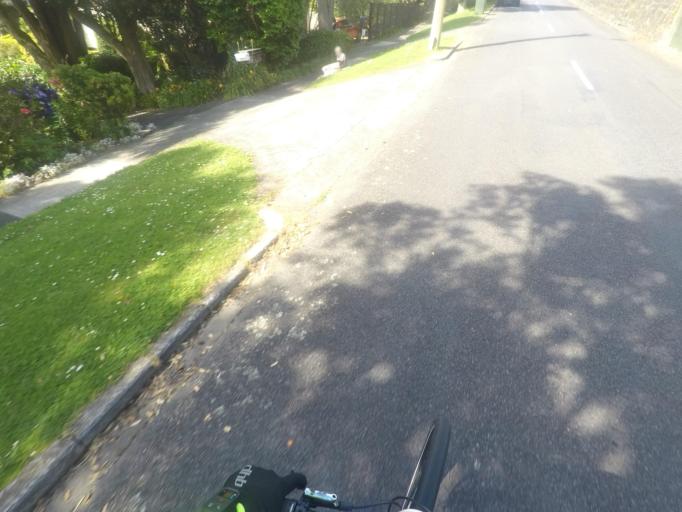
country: NZ
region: Auckland
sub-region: Auckland
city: Mangere
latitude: -36.9245
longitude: 174.7695
